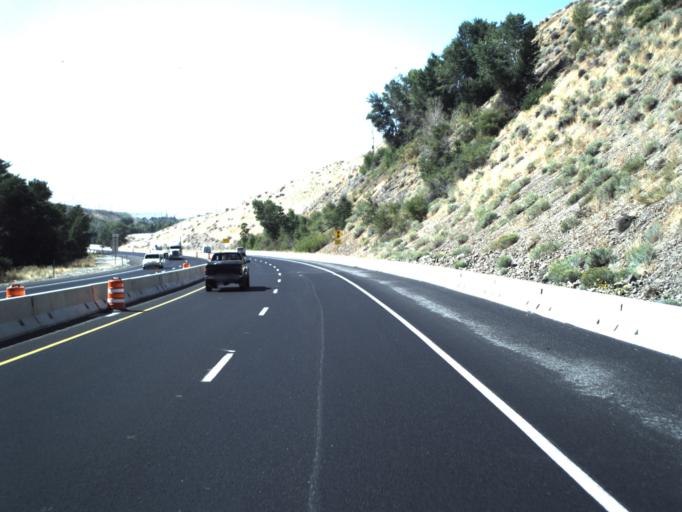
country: US
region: Utah
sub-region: Box Elder County
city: Brigham City
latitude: 41.4991
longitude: -111.9813
